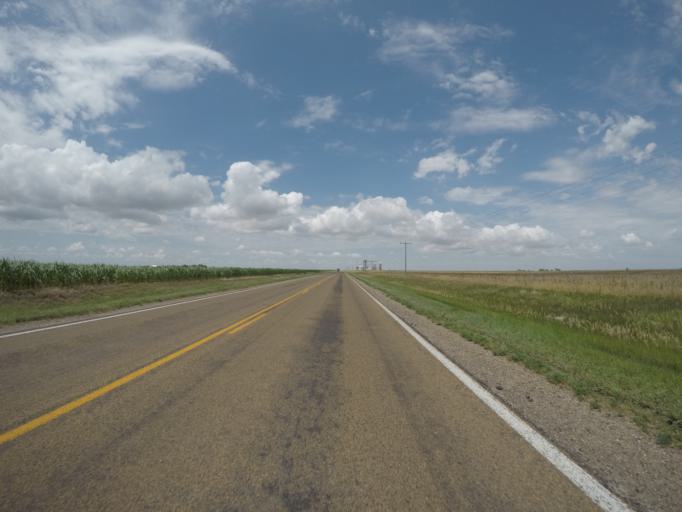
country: US
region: Kansas
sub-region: Rawlins County
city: Atwood
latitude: 39.8654
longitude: -101.0467
